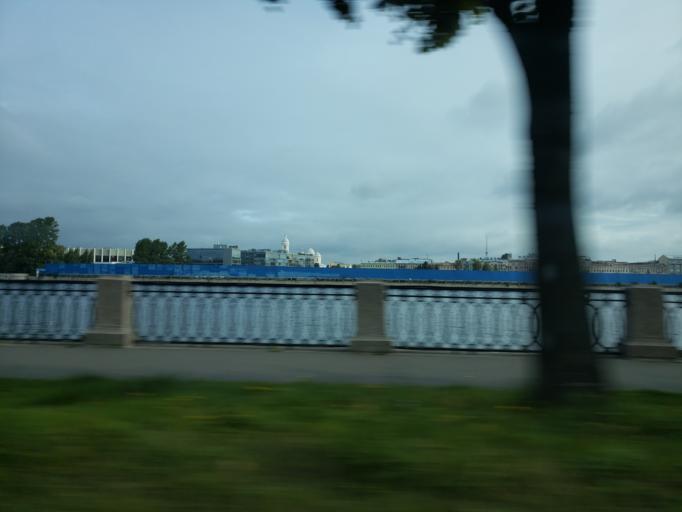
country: RU
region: St.-Petersburg
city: Saint Petersburg
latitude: 59.9456
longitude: 30.2946
